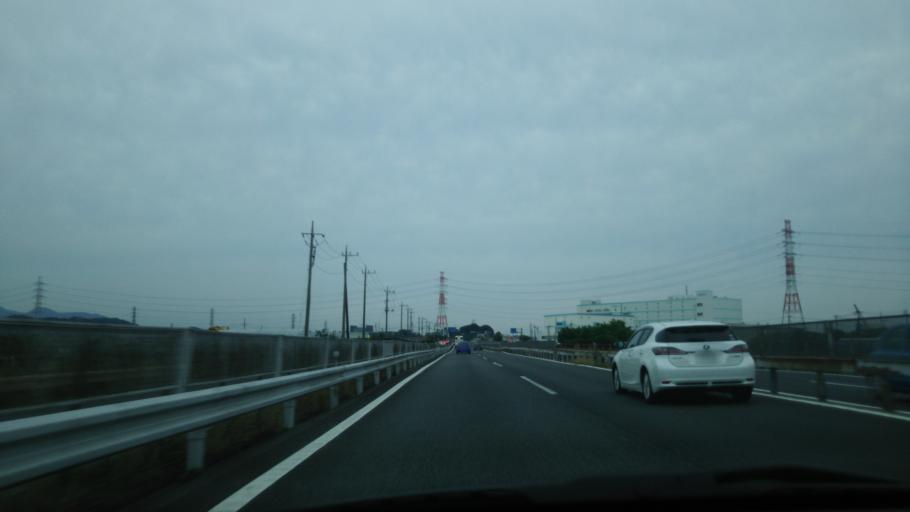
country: JP
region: Kanagawa
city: Isehara
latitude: 35.3987
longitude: 139.3347
